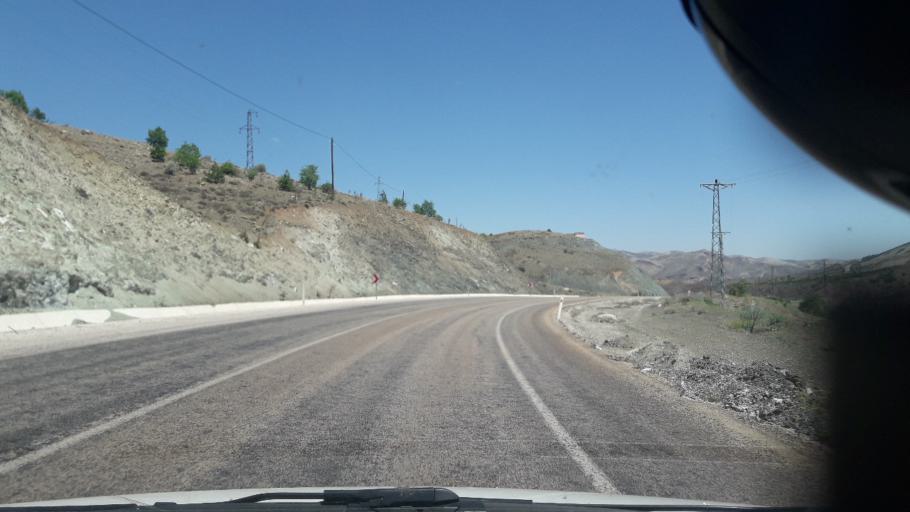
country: TR
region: Malatya
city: Hekimhan
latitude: 38.8219
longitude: 37.8771
